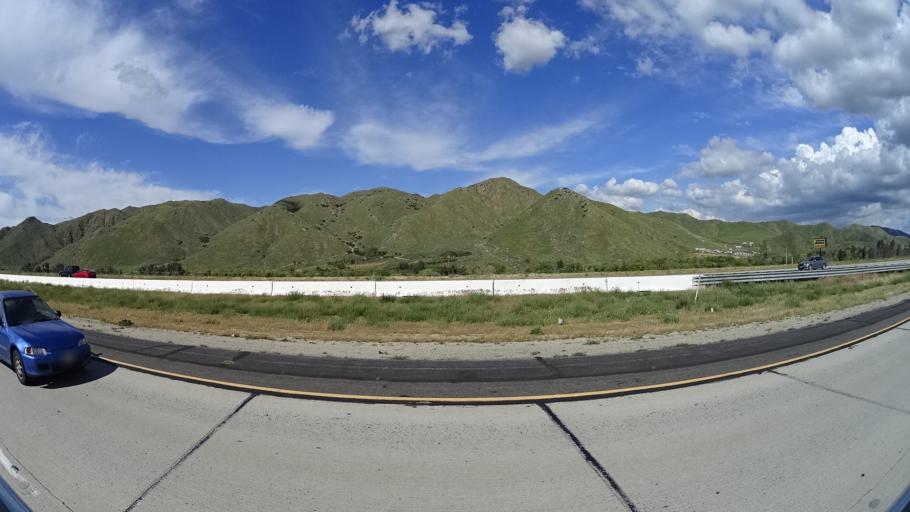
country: US
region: California
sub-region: Riverside County
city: Lake Elsinore
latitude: 33.7368
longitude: -117.4246
